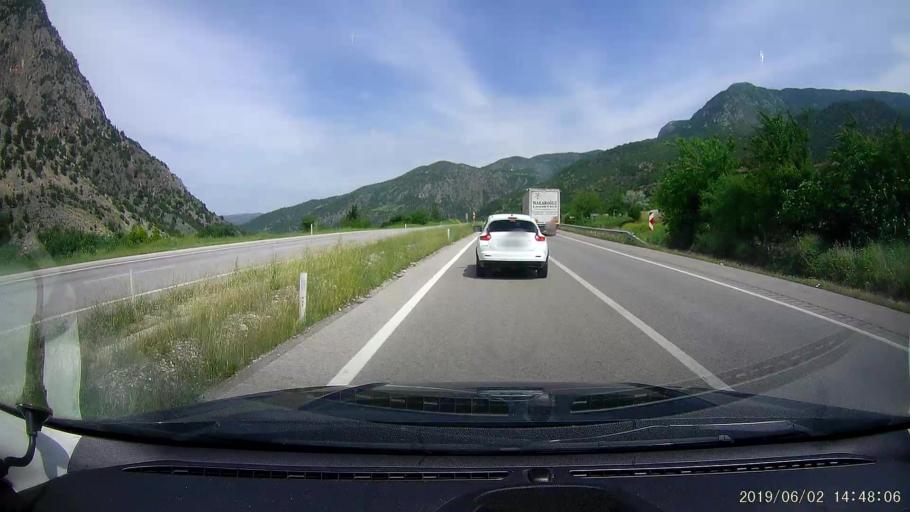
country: TR
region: Corum
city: Hacihamza
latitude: 41.0645
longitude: 34.4742
